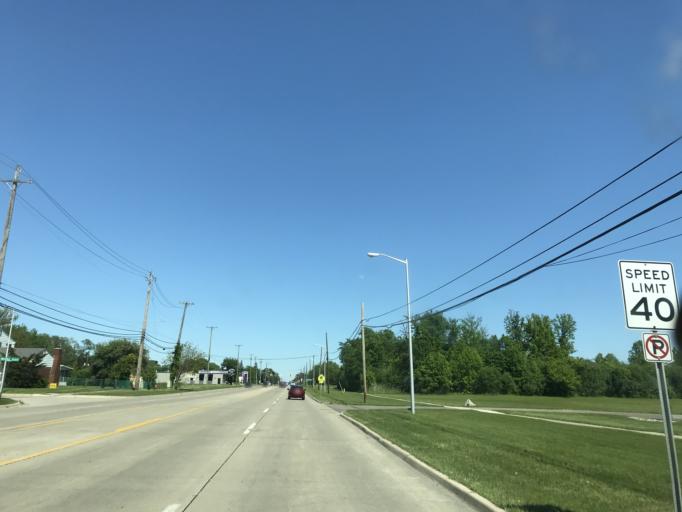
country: US
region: Michigan
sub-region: Wayne County
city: Riverview
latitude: 42.1845
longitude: -83.2127
